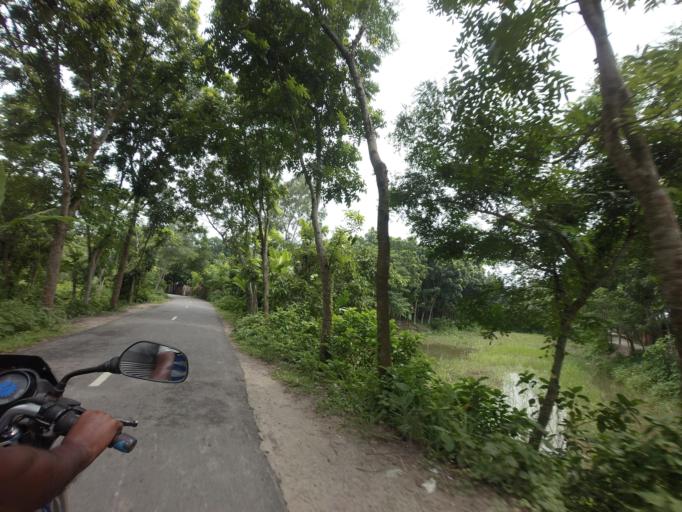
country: BD
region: Khulna
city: Kalia
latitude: 23.0968
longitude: 89.6531
